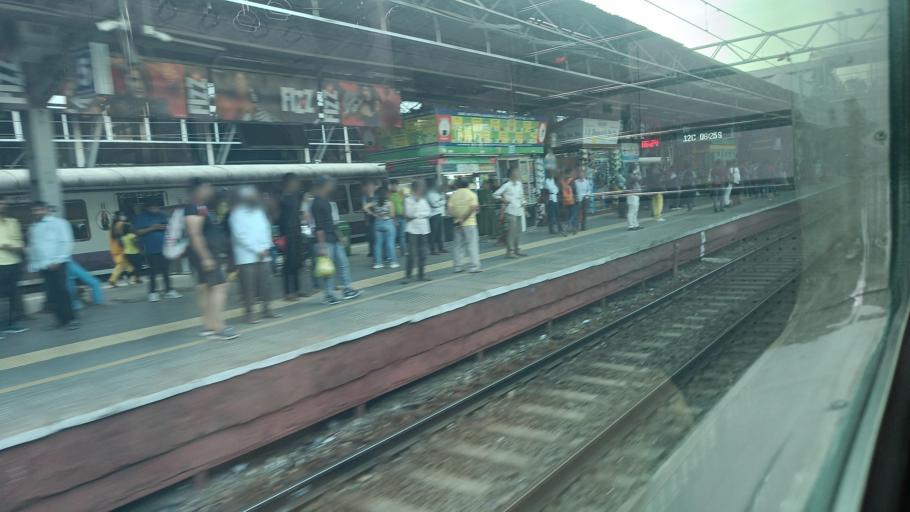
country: IN
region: Maharashtra
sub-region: Mumbai Suburban
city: Powai
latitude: 19.1186
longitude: 72.8467
